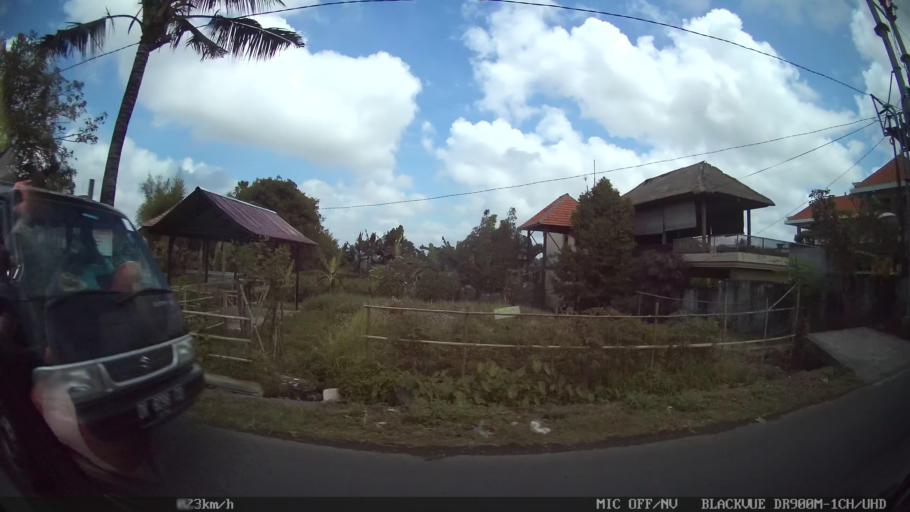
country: ID
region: Bali
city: Banjar Desa
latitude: -8.5731
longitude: 115.2864
